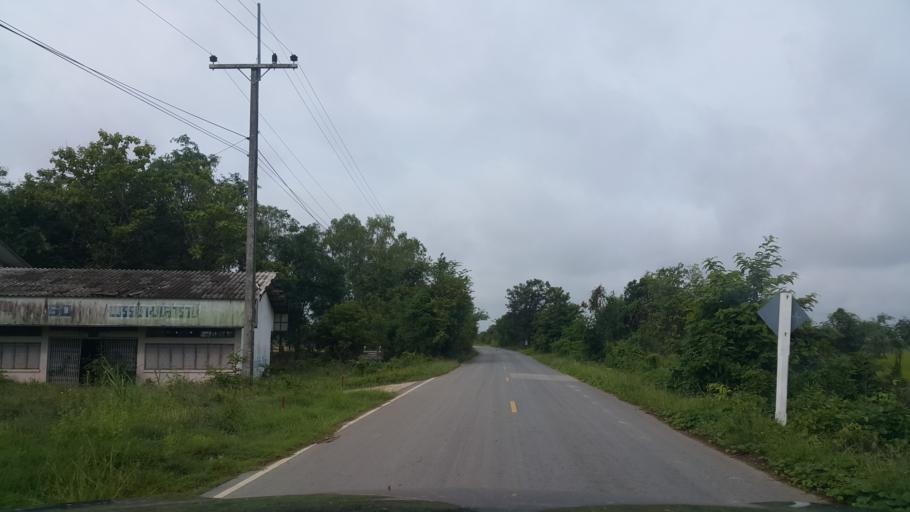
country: TH
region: Sukhothai
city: Sawankhalok
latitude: 17.3132
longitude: 99.6999
